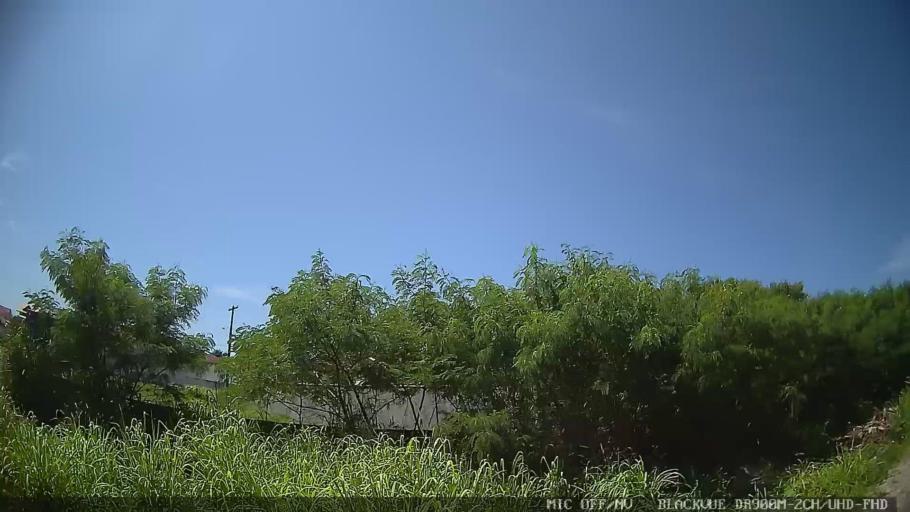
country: BR
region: Sao Paulo
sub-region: Peruibe
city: Peruibe
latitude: -24.2990
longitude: -46.9747
